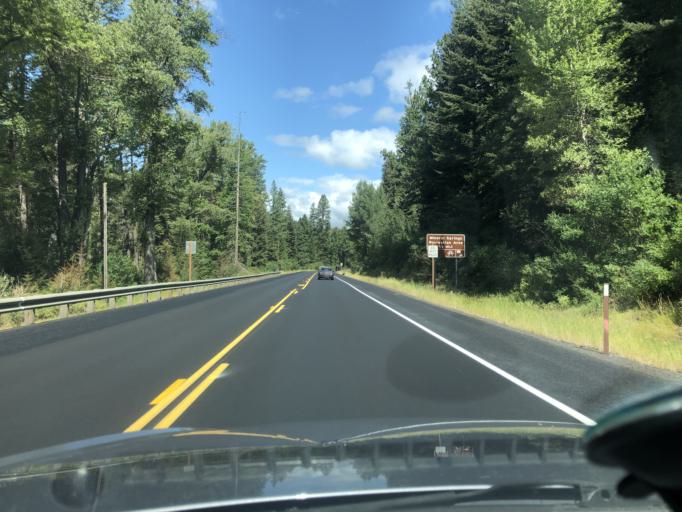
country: US
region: Washington
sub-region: Kittitas County
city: Cle Elum
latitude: 47.2811
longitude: -120.6978
